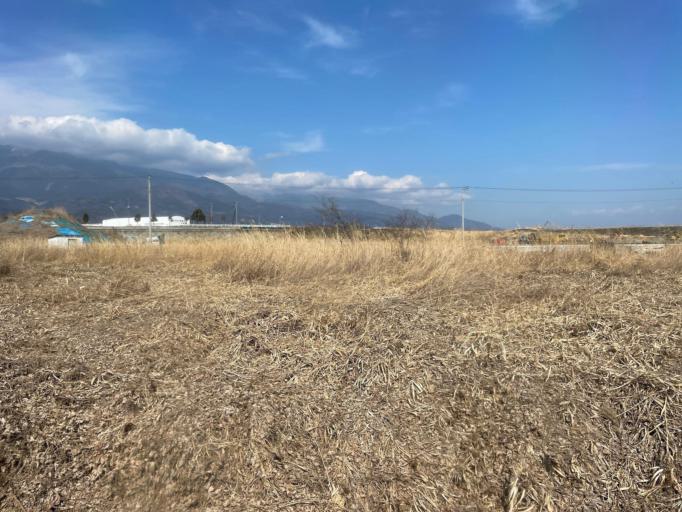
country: JP
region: Yamanashi
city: Ryuo
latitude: 35.5545
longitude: 138.4839
